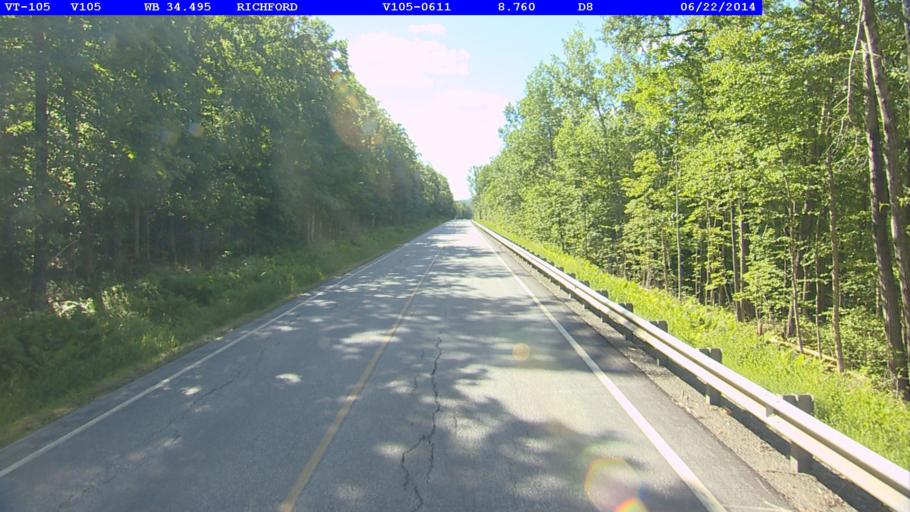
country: US
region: Vermont
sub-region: Franklin County
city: Richford
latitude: 44.9892
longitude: -72.5577
